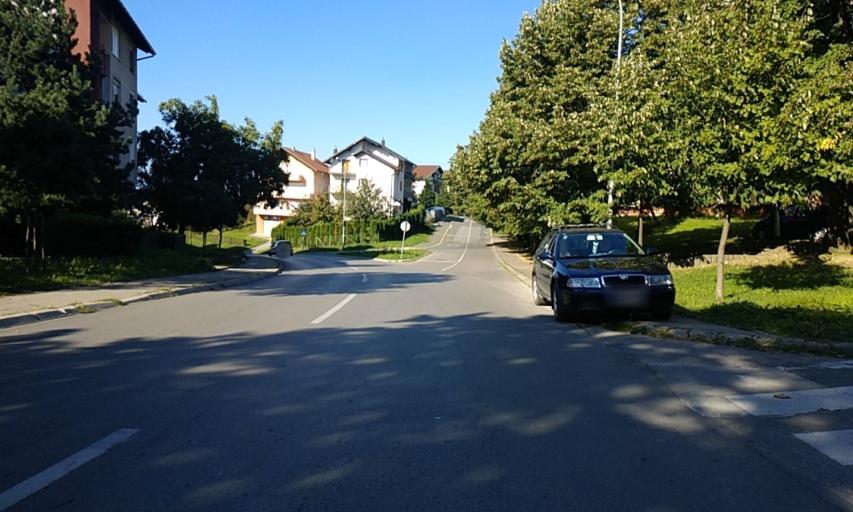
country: BA
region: Republika Srpska
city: Starcevica
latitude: 44.7600
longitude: 17.2118
